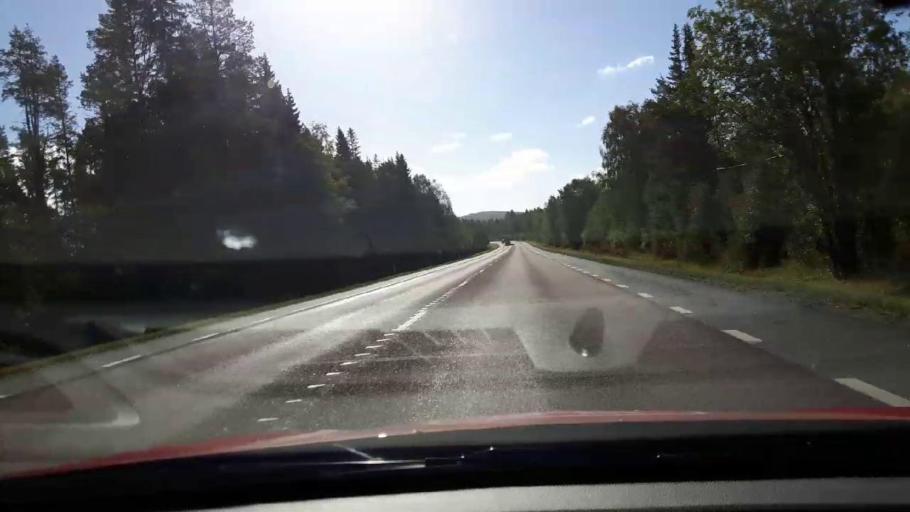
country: SE
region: Jaemtland
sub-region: Braecke Kommun
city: Braecke
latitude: 62.8218
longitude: 15.3294
